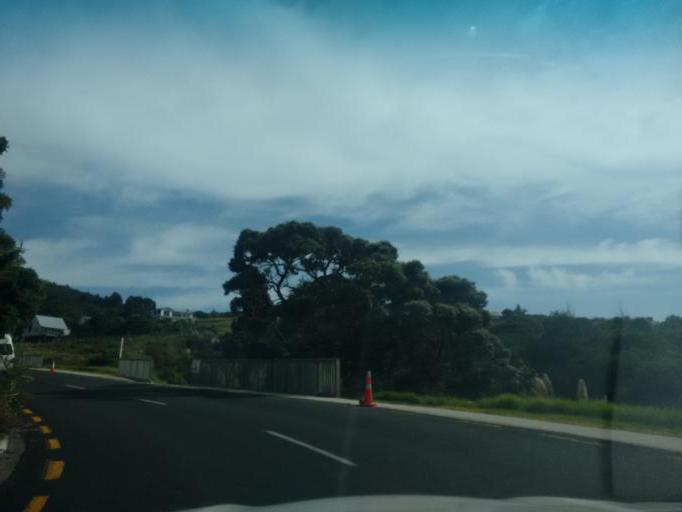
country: NZ
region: Waikato
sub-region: Thames-Coromandel District
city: Whitianga
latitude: -36.8373
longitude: 175.8006
